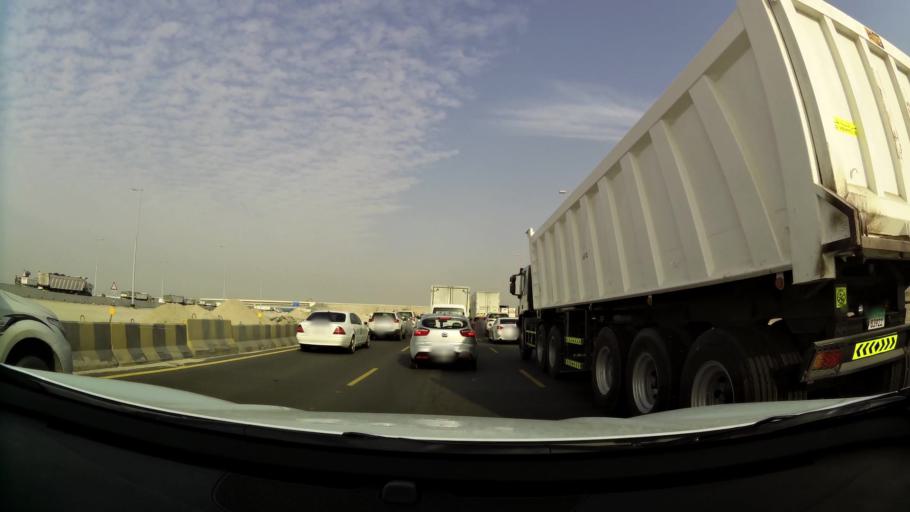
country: AE
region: Abu Dhabi
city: Abu Dhabi
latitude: 24.2842
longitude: 54.5446
